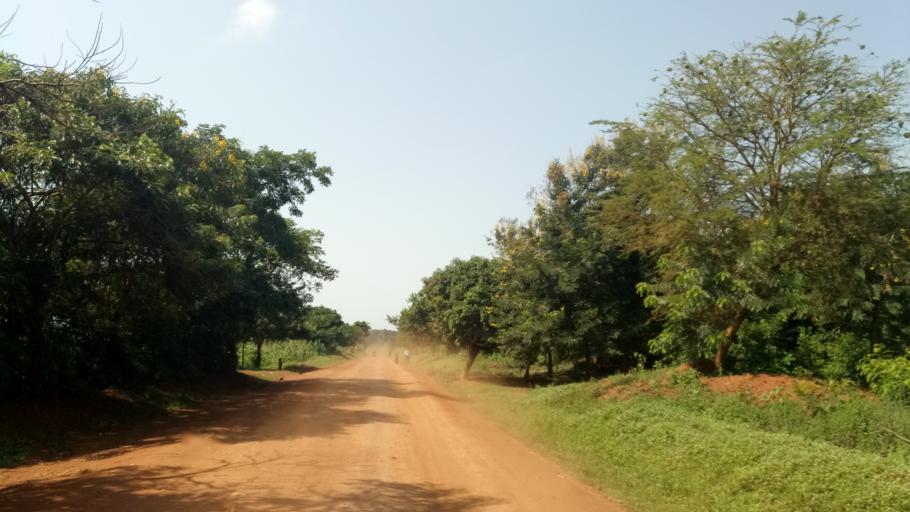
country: UG
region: Eastern Region
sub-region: Kaliro District
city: Kaliro
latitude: 0.9778
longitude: 33.4582
